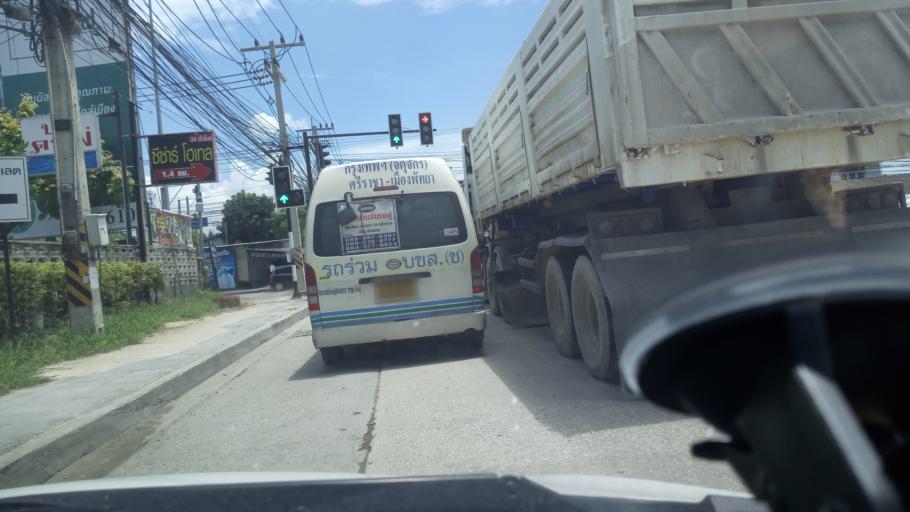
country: TH
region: Chon Buri
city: Chon Buri
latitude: 13.4010
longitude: 101.0309
